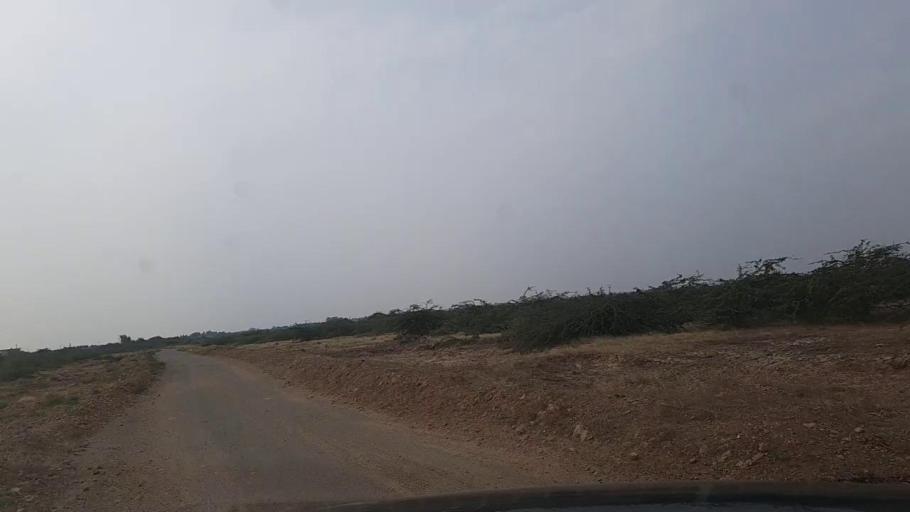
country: PK
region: Sindh
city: Thatta
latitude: 24.8074
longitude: 67.9115
